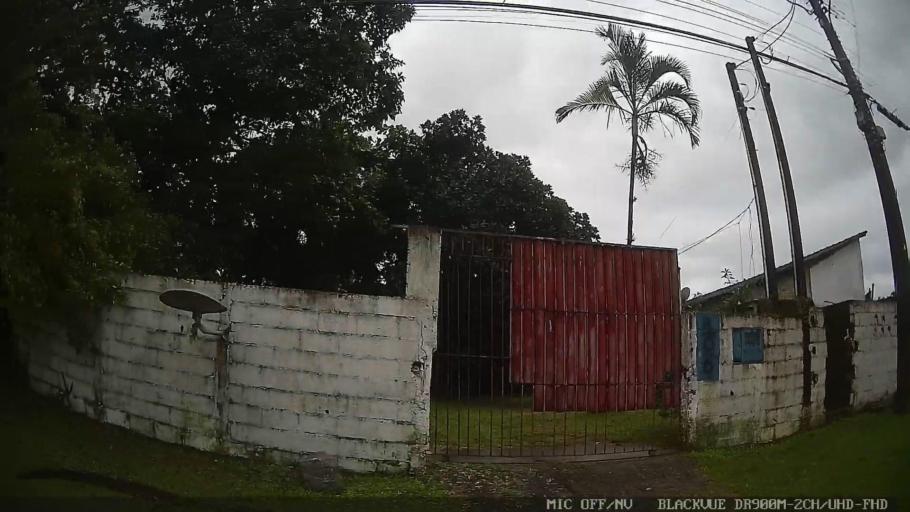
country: BR
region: Sao Paulo
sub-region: Itanhaem
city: Itanhaem
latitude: -24.1768
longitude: -46.8295
